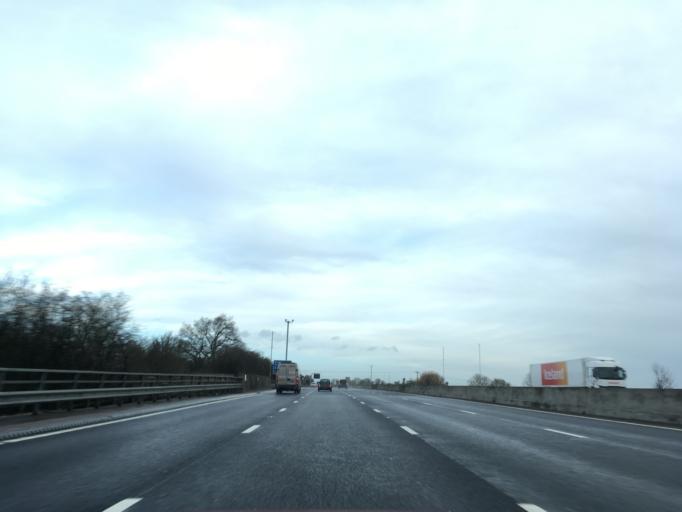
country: GB
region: England
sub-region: Worcestershire
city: Droitwich
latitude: 52.2746
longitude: -2.1221
